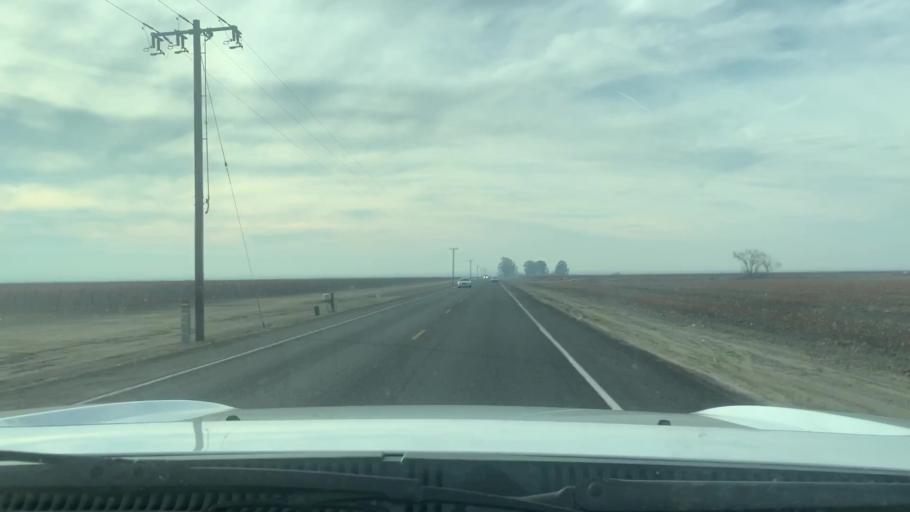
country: US
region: California
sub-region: Kern County
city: Buttonwillow
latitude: 35.4996
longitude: -119.5697
